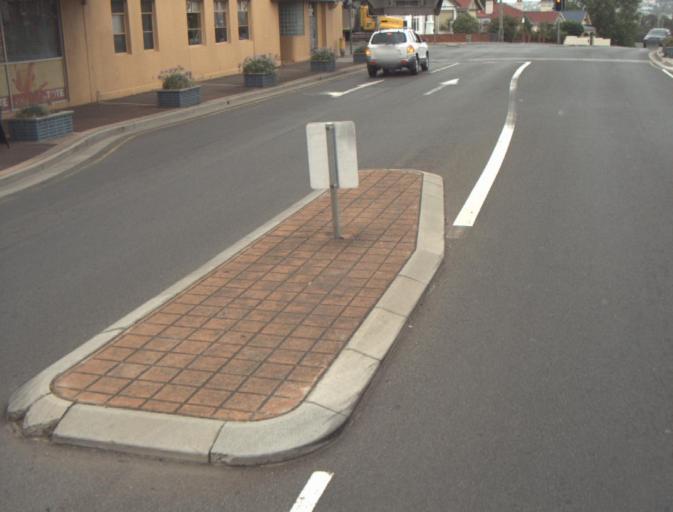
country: AU
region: Tasmania
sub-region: Launceston
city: Newnham
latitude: -41.4062
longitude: 147.1331
